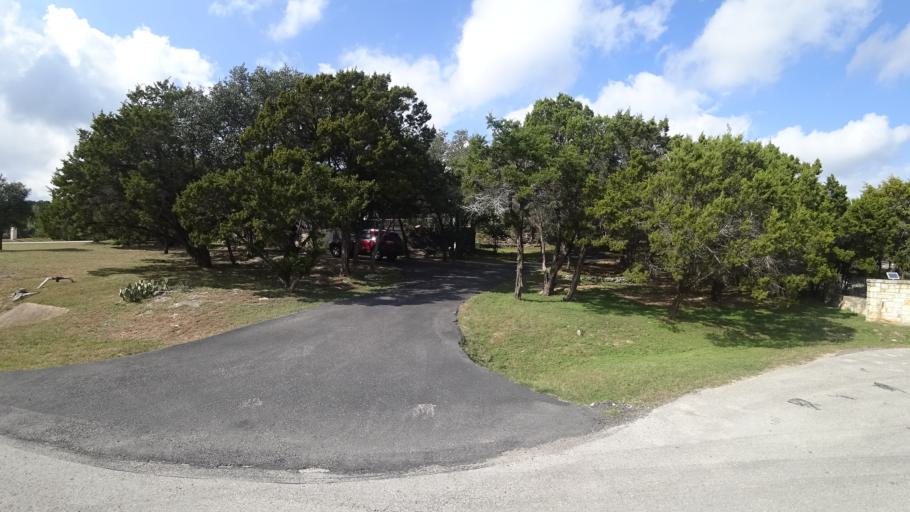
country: US
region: Texas
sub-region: Travis County
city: Barton Creek
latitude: 30.3024
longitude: -97.8712
